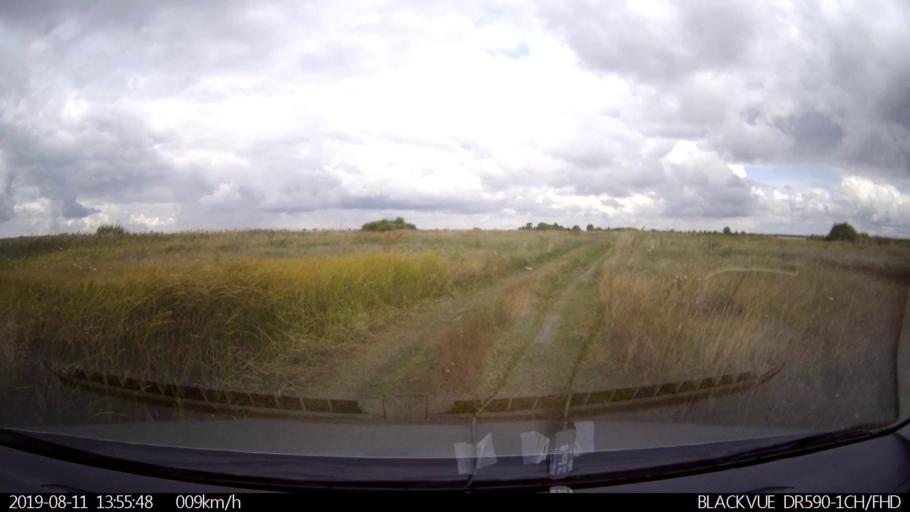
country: RU
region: Ulyanovsk
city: Ignatovka
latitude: 53.8461
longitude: 47.5873
